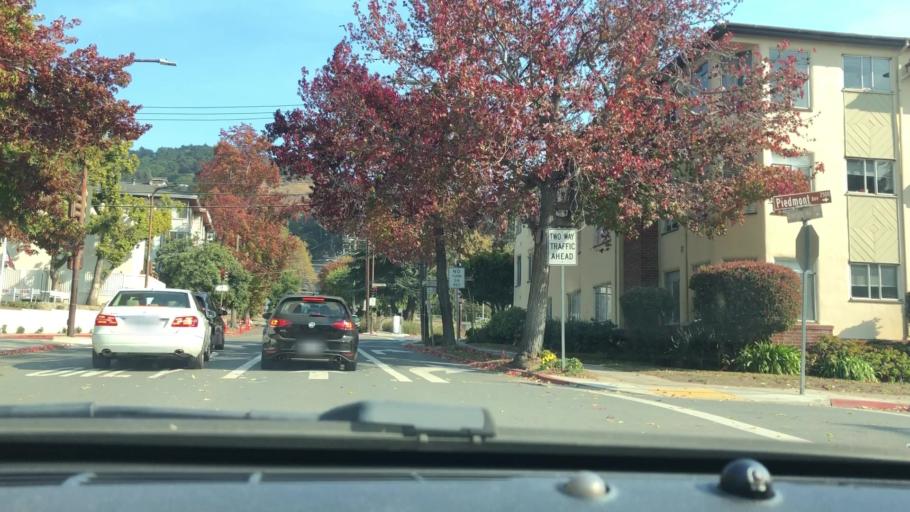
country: US
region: California
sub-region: Alameda County
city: Berkeley
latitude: 37.8659
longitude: -122.2517
